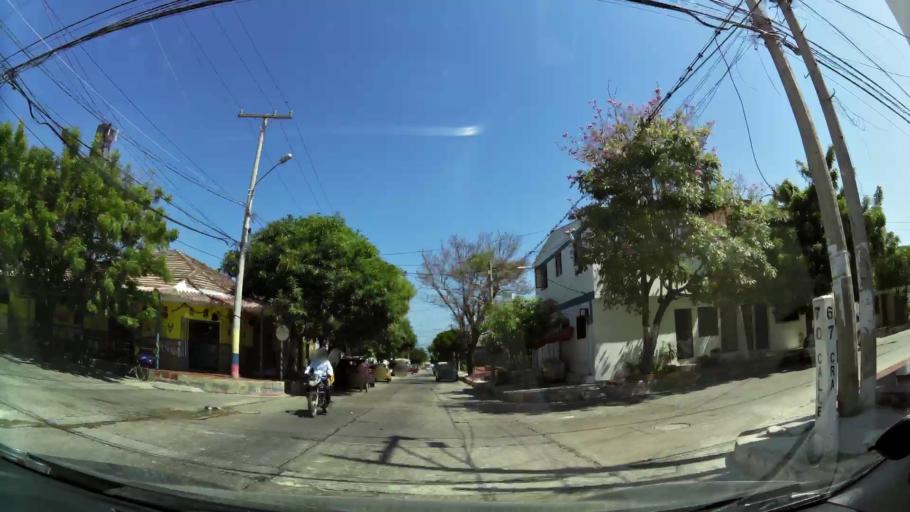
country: CO
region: Atlantico
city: Barranquilla
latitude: 11.0044
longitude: -74.7923
